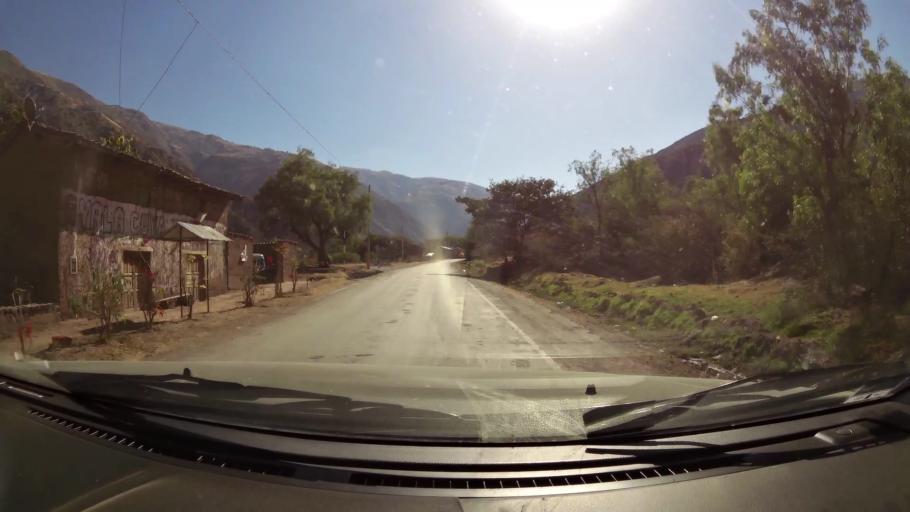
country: PE
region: Huancavelica
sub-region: Provincia de Acobamba
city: Pomacocha
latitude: -12.7680
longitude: -74.5049
